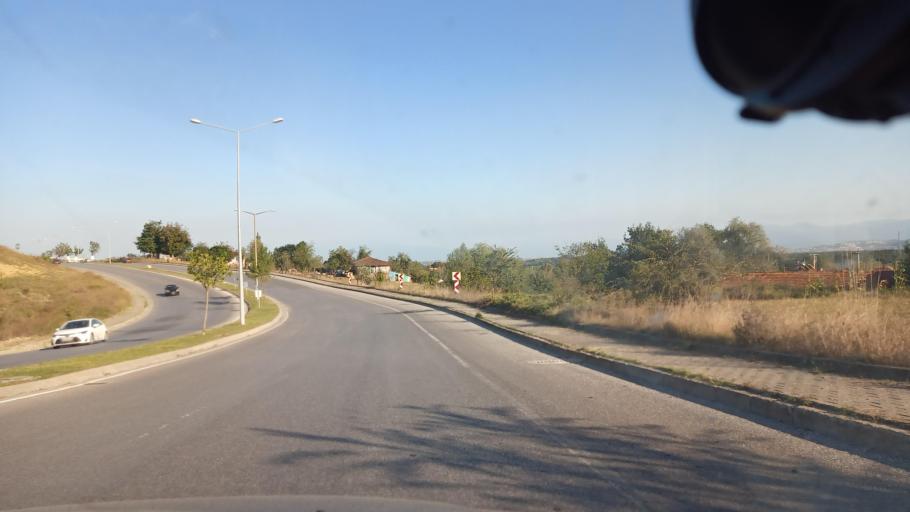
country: TR
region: Sakarya
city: Kazimpasa
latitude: 40.8532
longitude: 30.3006
